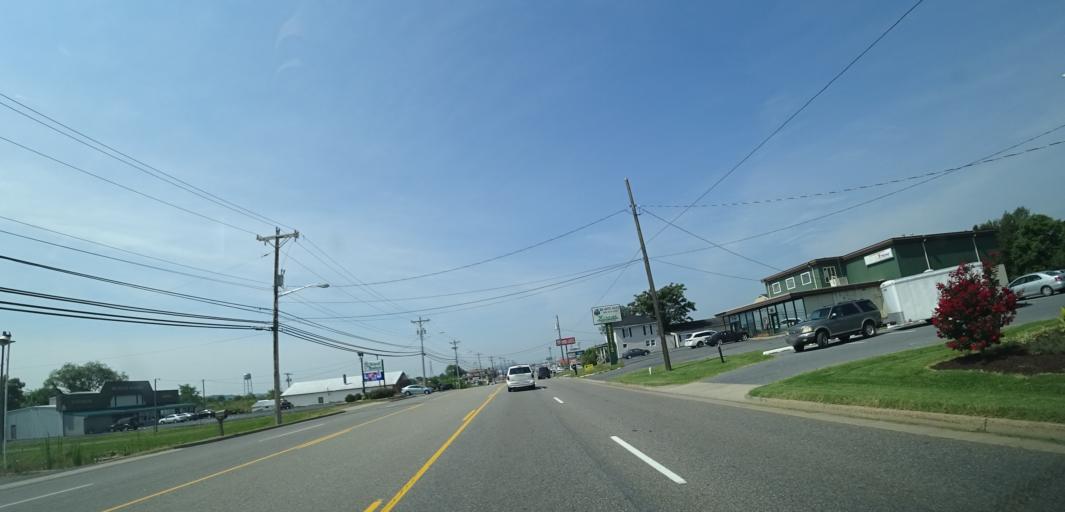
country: US
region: Virginia
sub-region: Rockingham County
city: Dayton
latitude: 38.4125
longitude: -78.9016
